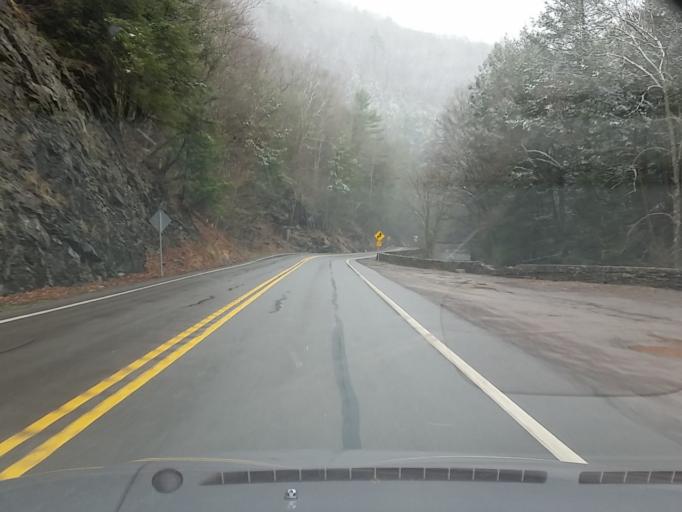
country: US
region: Pennsylvania
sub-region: Luzerne County
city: Nanticoke
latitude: 41.2514
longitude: -75.9983
